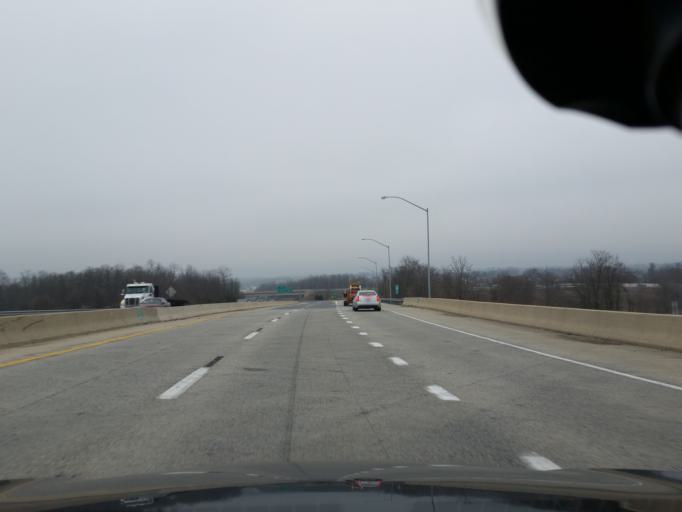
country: US
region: Pennsylvania
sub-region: Cumberland County
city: Shiremanstown
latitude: 40.2404
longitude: -76.9790
